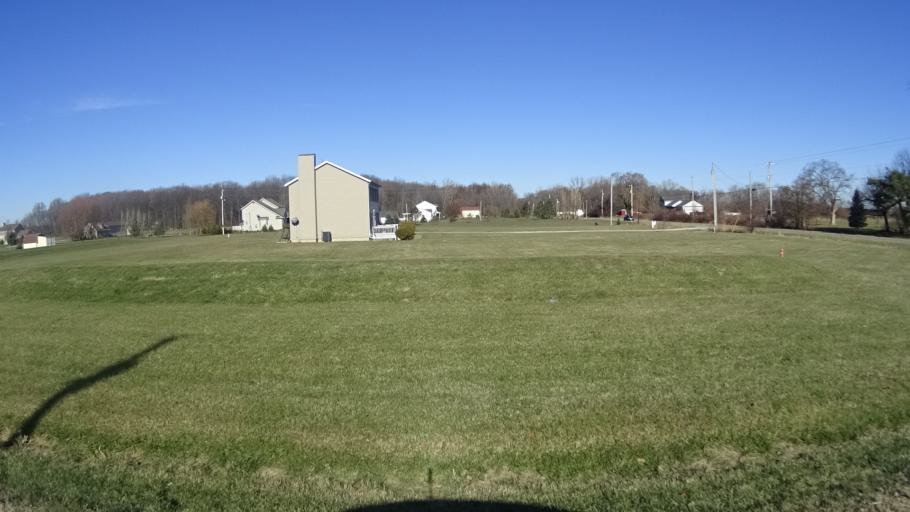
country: US
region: Ohio
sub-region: Lorain County
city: Camden
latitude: 41.2872
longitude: -82.2887
